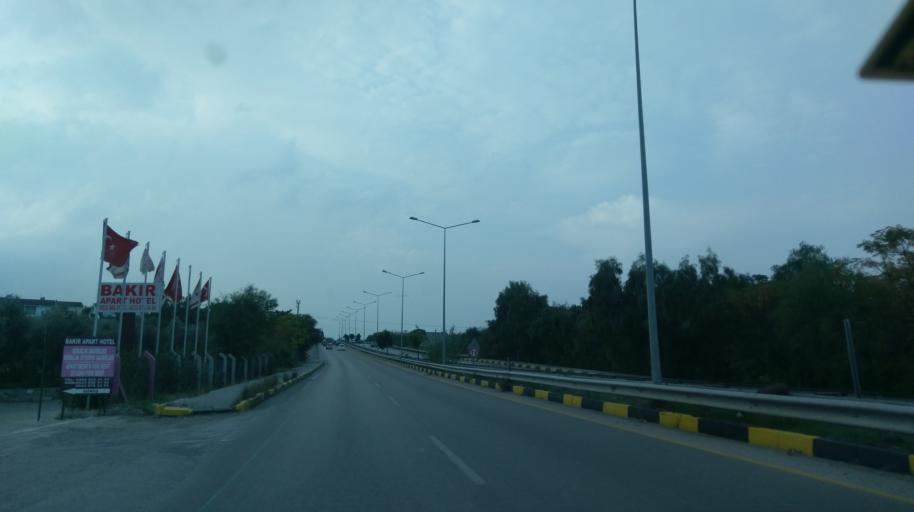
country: CY
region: Keryneia
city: Kyrenia
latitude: 35.3350
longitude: 33.2616
